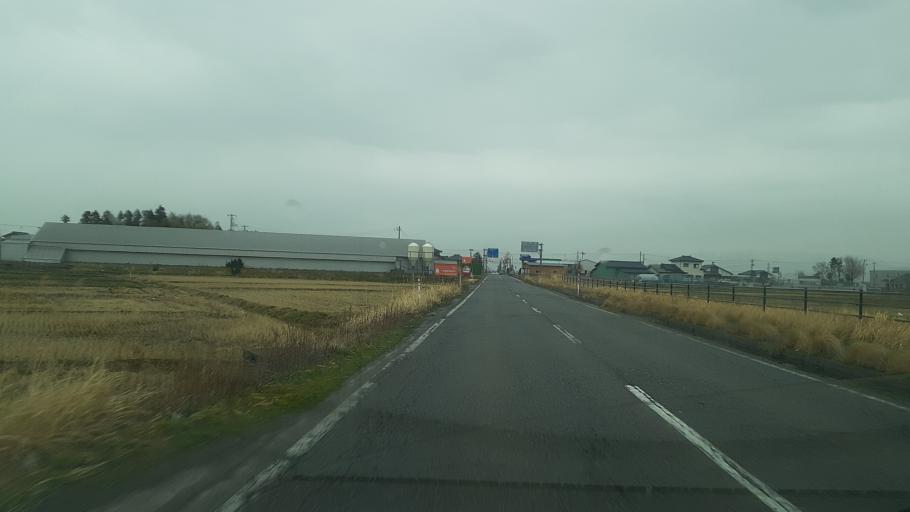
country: JP
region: Niigata
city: Kameda-honcho
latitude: 37.8838
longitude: 139.1745
